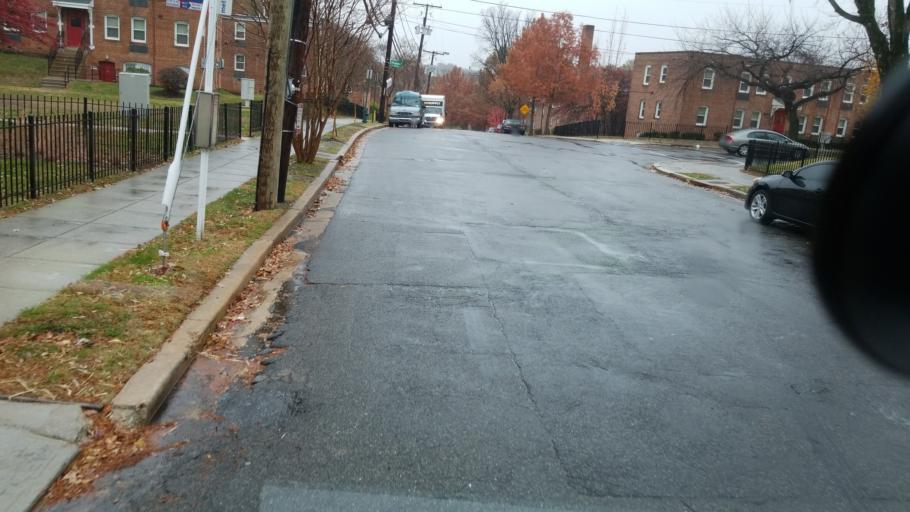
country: US
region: Maryland
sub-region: Prince George's County
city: Coral Hills
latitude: 38.8832
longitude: -76.9402
